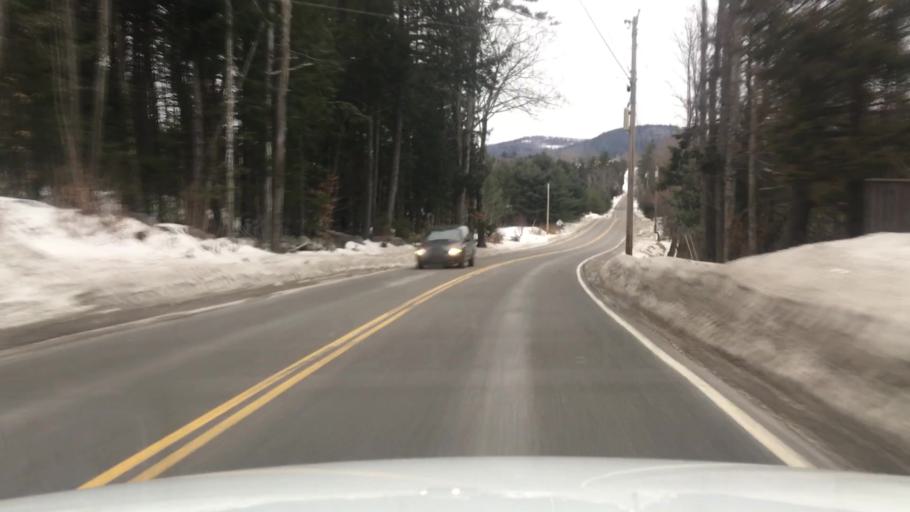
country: US
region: Maine
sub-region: York County
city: Limerick
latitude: 43.7089
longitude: -70.8111
